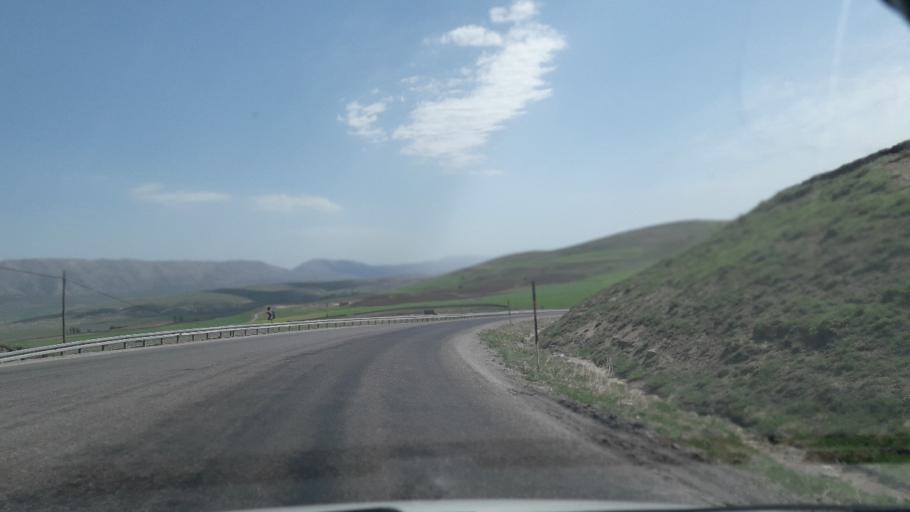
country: TR
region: Sivas
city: Deliktas
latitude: 39.3393
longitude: 37.1433
